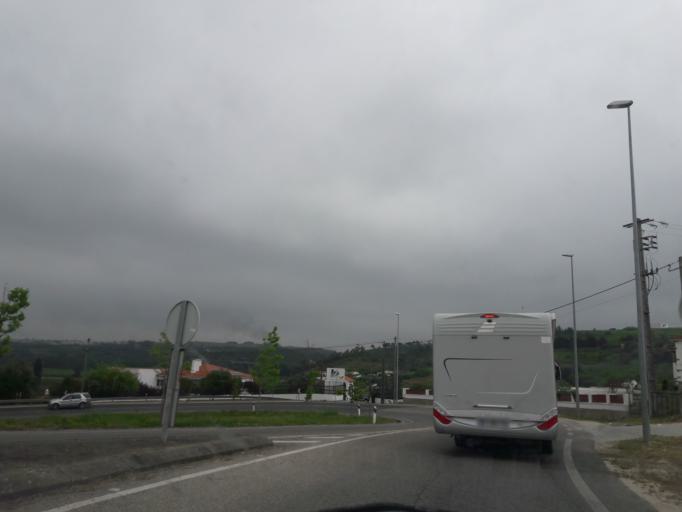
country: PT
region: Leiria
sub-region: Obidos
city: Obidos
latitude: 39.3579
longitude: -9.1530
